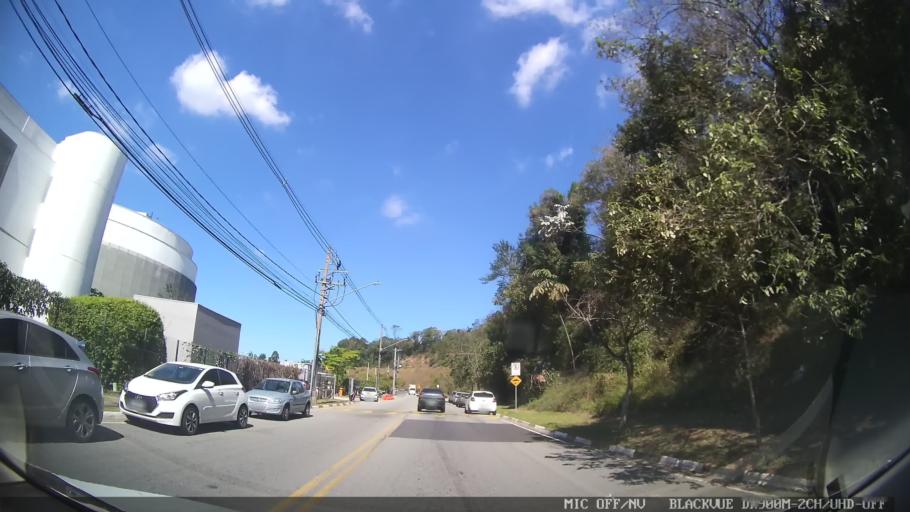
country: BR
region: Sao Paulo
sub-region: Carapicuiba
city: Carapicuiba
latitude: -23.4630
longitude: -46.8328
